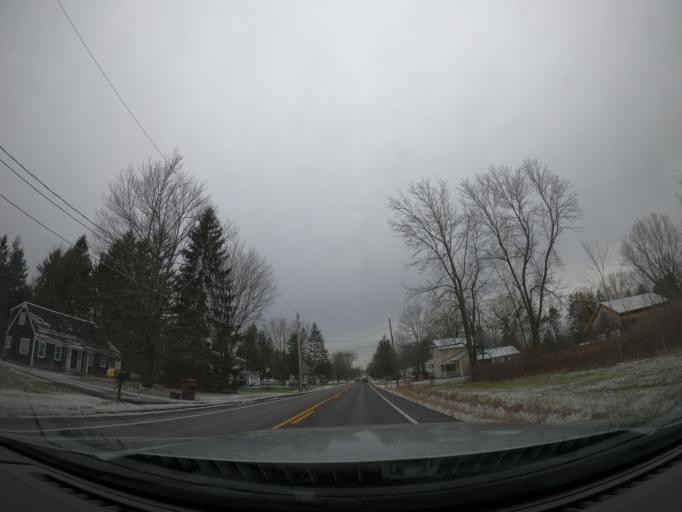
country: US
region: New York
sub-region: Onondaga County
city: Minoa
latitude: 43.1149
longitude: -76.0065
